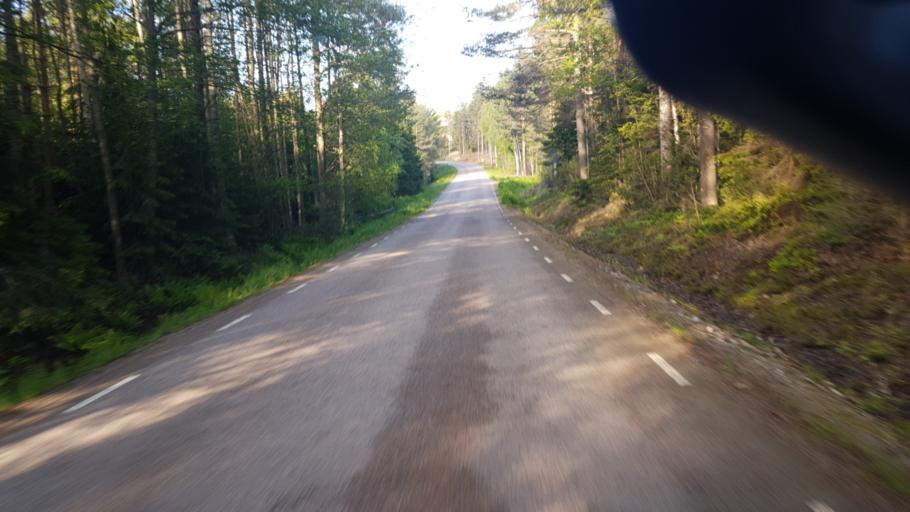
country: SE
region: Vaermland
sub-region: Arvika Kommun
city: Arvika
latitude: 59.5422
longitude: 12.5186
